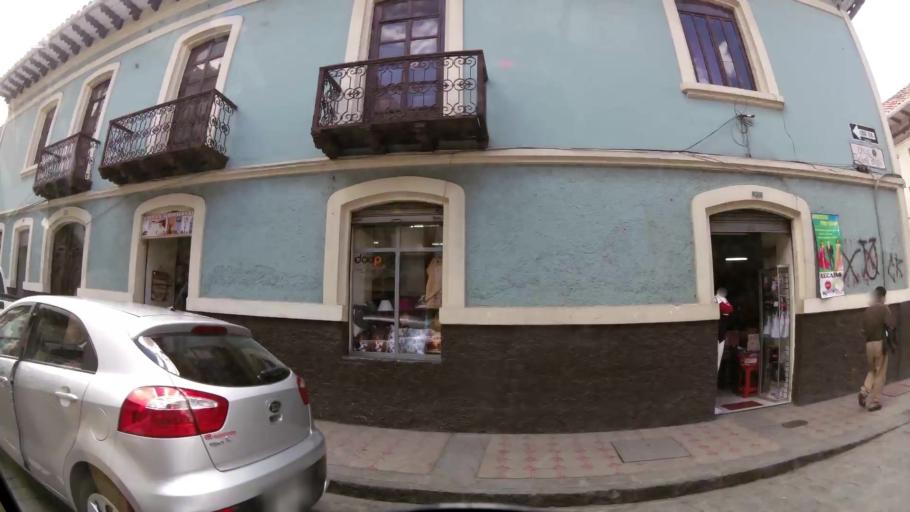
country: EC
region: Azuay
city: Cuenca
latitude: -2.8934
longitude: -79.0022
